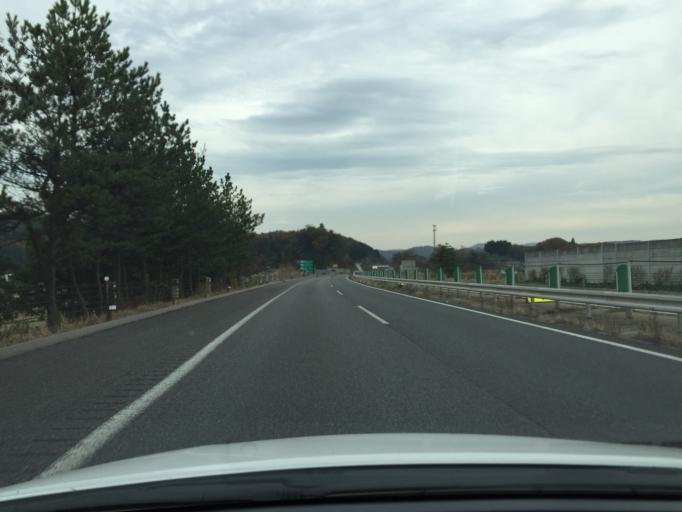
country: JP
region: Fukushima
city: Fukushima-shi
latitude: 37.7289
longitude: 140.4261
